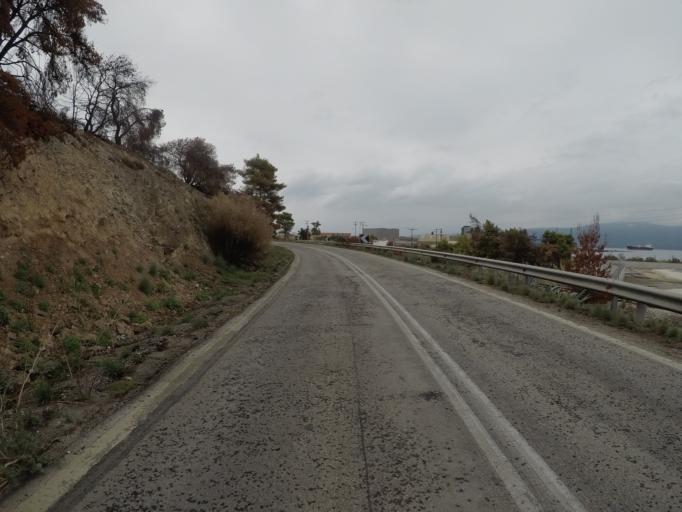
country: GR
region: Peloponnese
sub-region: Nomos Korinthias
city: Isthmia
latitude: 37.9213
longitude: 23.0552
